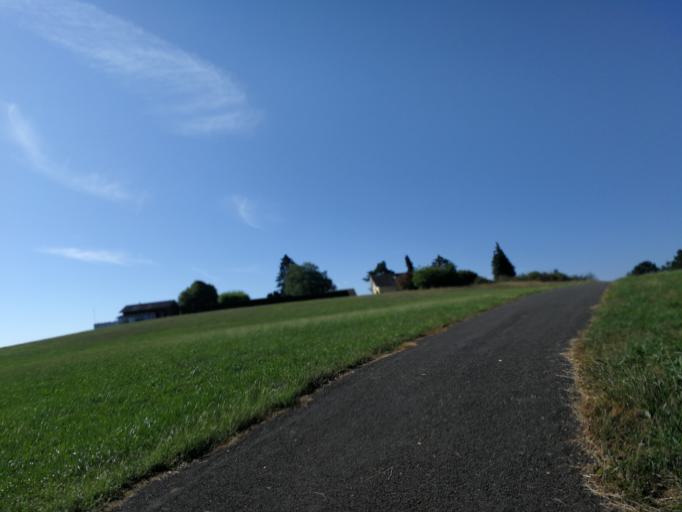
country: CH
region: Zurich
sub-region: Bezirk Hinwil
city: Durnten
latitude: 47.2737
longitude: 8.8327
